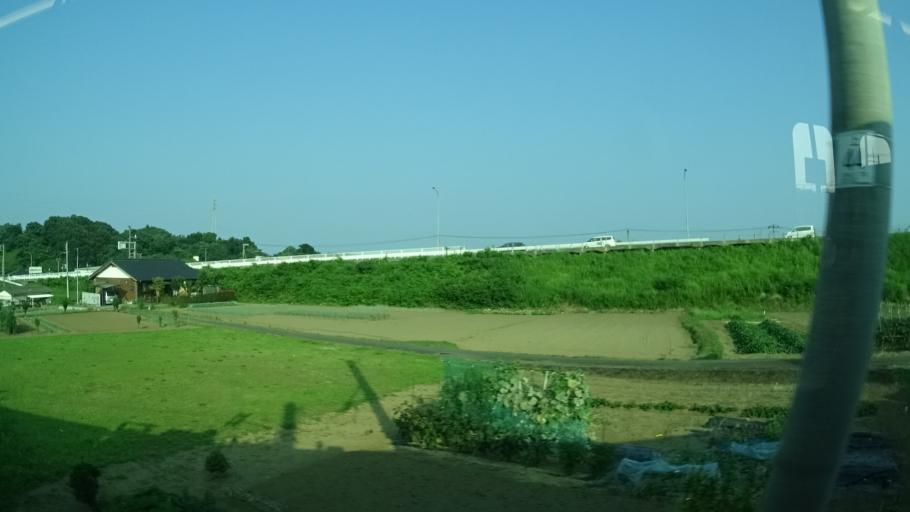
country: JP
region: Ibaraki
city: Hitachi
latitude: 36.6154
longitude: 140.6718
